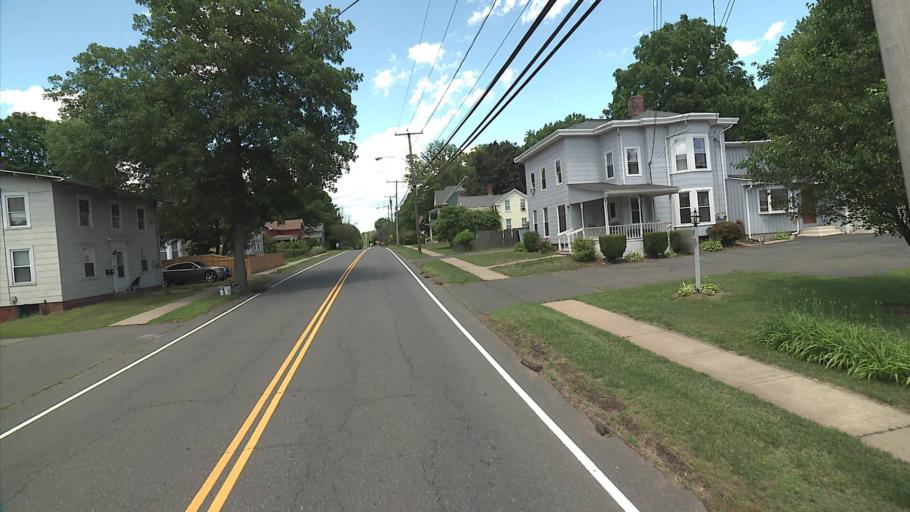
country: US
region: Connecticut
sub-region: Hartford County
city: Hazardville
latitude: 41.9885
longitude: -72.5393
